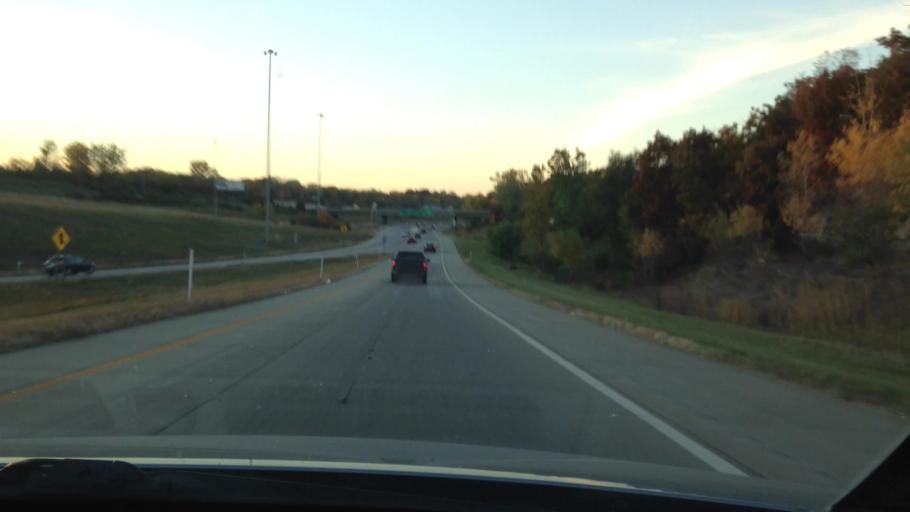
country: US
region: Kansas
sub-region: Wyandotte County
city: Kansas City
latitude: 39.1063
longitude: -94.6773
